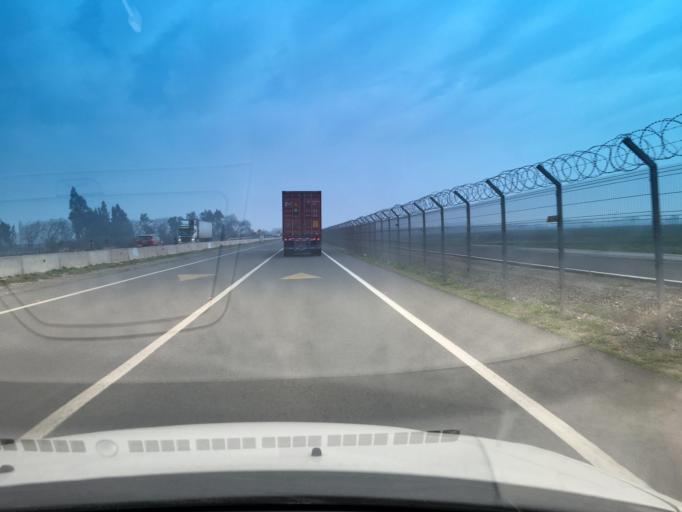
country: CL
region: Santiago Metropolitan
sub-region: Provincia de Santiago
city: Lo Prado
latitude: -33.3715
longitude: -70.8054
